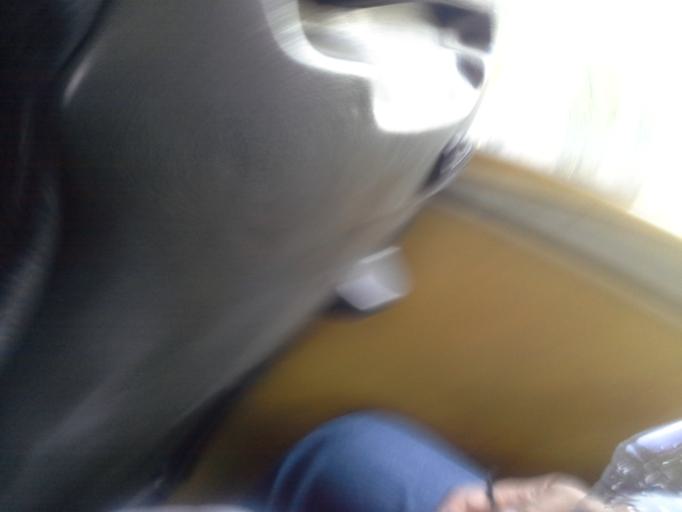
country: IN
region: Telangana
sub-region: Hyderabad
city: Hyderabad
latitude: 17.3890
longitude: 78.3515
